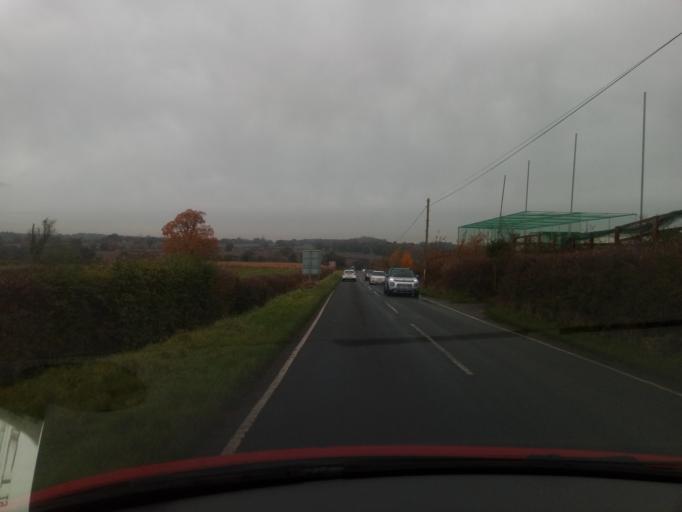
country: GB
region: England
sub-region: Derbyshire
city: Borrowash
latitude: 52.9282
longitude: -1.4050
